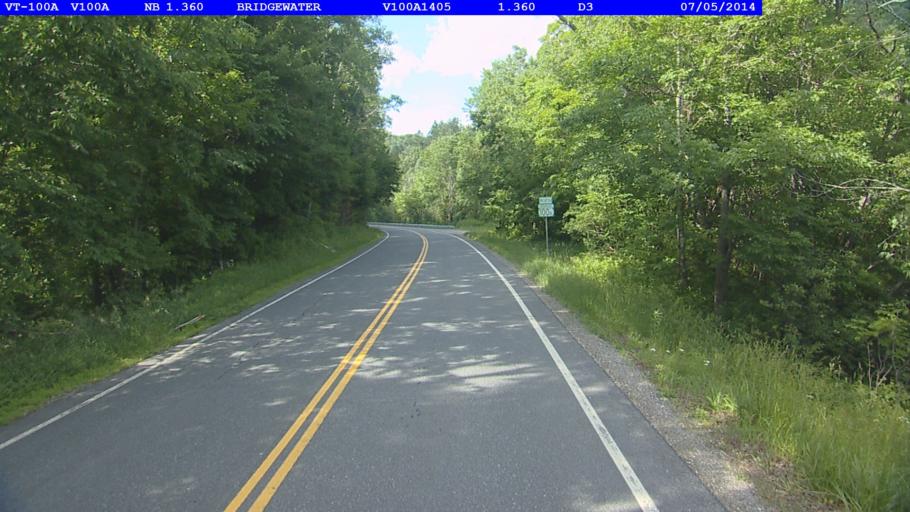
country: US
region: Vermont
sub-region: Windsor County
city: Woodstock
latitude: 43.5378
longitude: -72.7183
